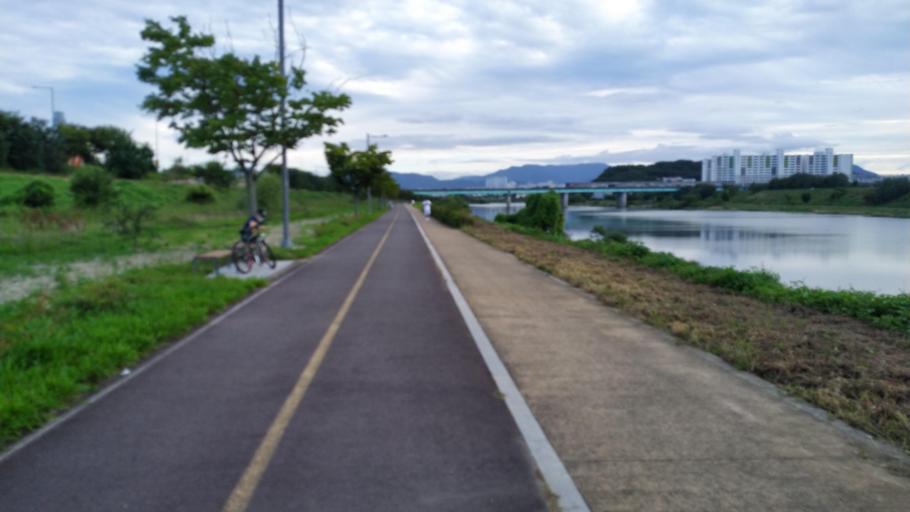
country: KR
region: Daegu
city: Daegu
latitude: 35.9228
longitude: 128.6327
